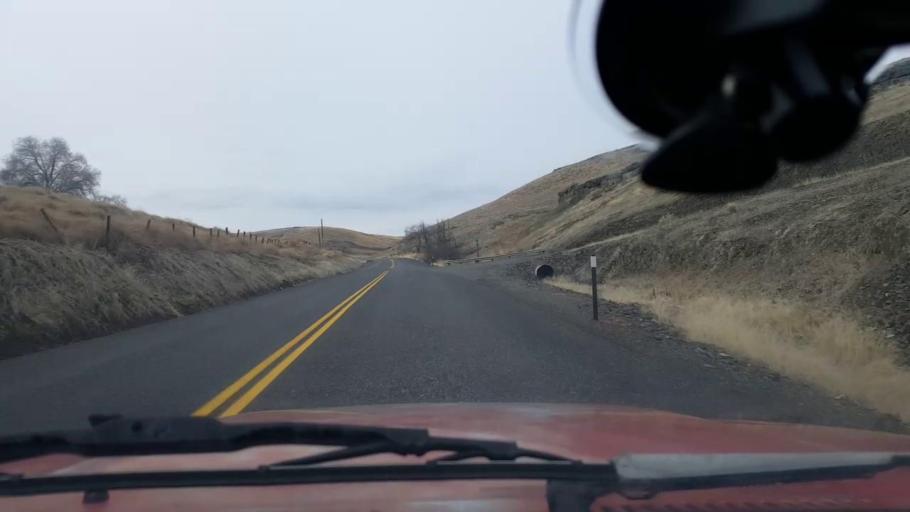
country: US
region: Washington
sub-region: Asotin County
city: Clarkston Heights-Vineland
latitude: 46.3825
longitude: -117.1316
